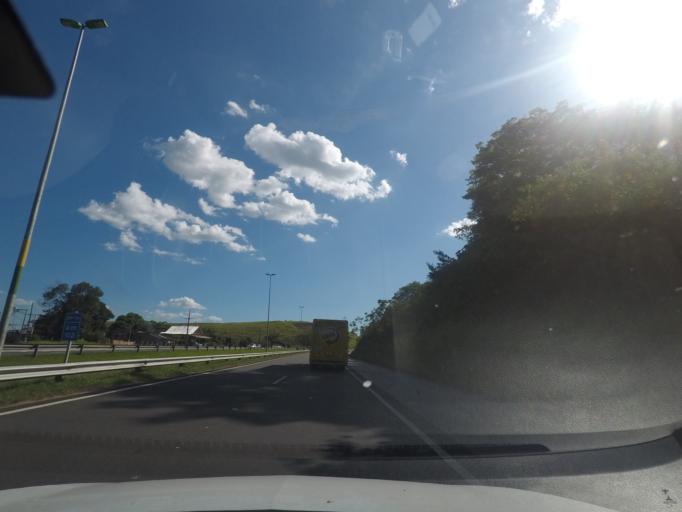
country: BR
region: Rio de Janeiro
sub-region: Guapimirim
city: Guapimirim
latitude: -22.5905
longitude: -43.0203
